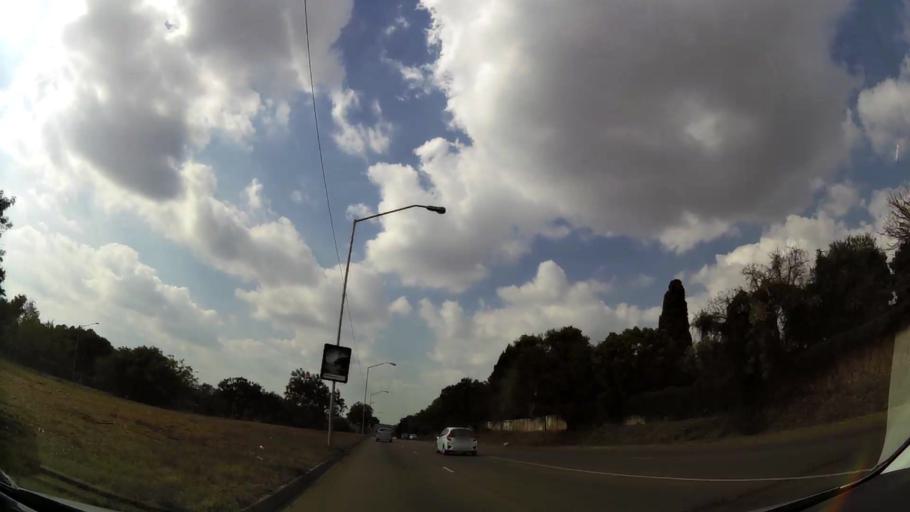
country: ZA
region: Gauteng
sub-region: City of Tshwane Metropolitan Municipality
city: Pretoria
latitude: -25.7837
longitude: 28.2943
